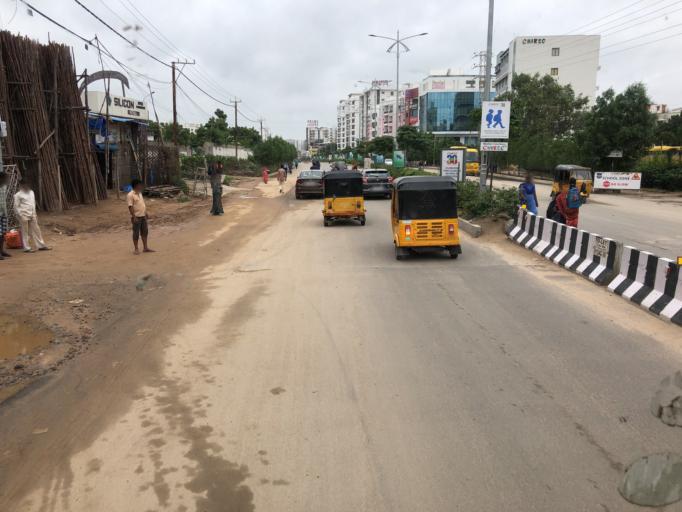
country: IN
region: Telangana
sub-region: Medak
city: Serilingampalle
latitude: 17.4615
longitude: 78.3521
